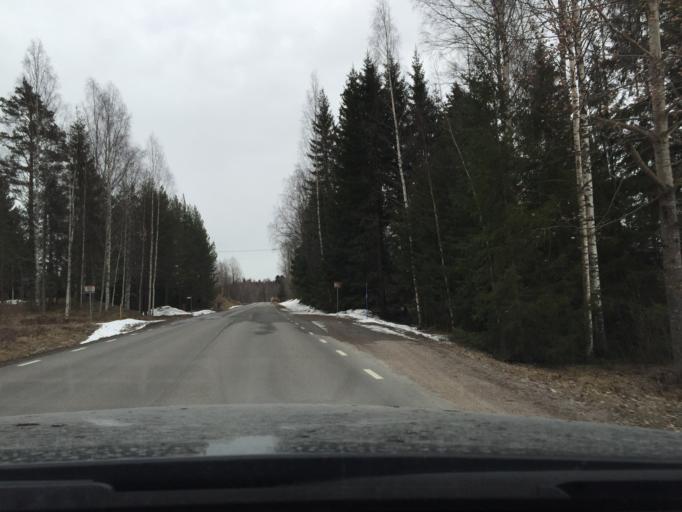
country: SE
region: Gaevleborg
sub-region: Sandvikens Kommun
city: Jarbo
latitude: 60.7621
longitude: 16.5246
